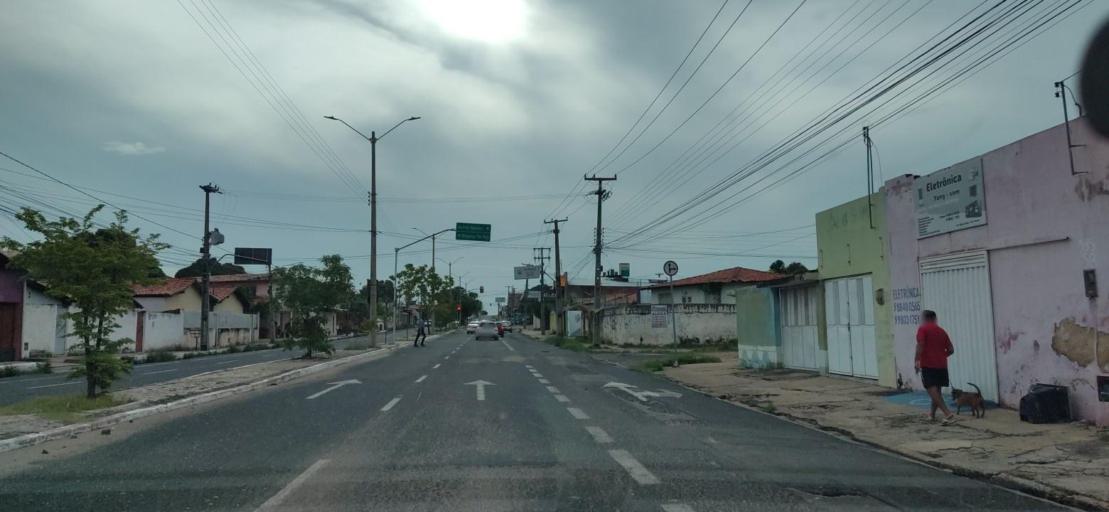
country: BR
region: Piaui
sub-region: Teresina
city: Teresina
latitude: -5.0953
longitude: -42.7921
